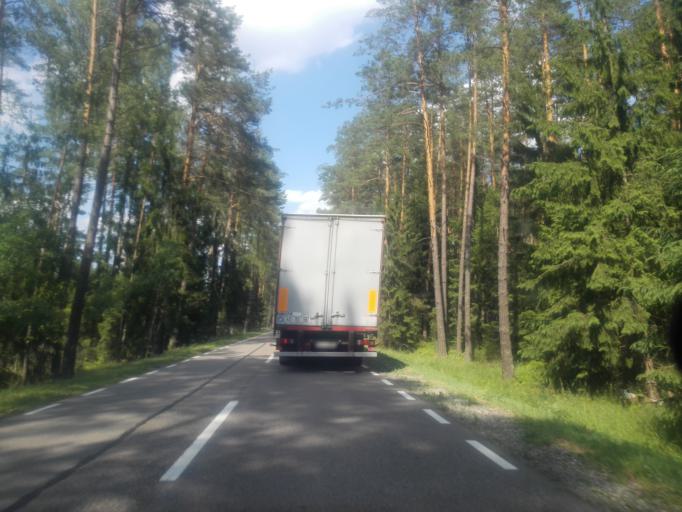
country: PL
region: Podlasie
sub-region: Powiat augustowski
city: Augustow
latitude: 53.8924
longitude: 23.1201
